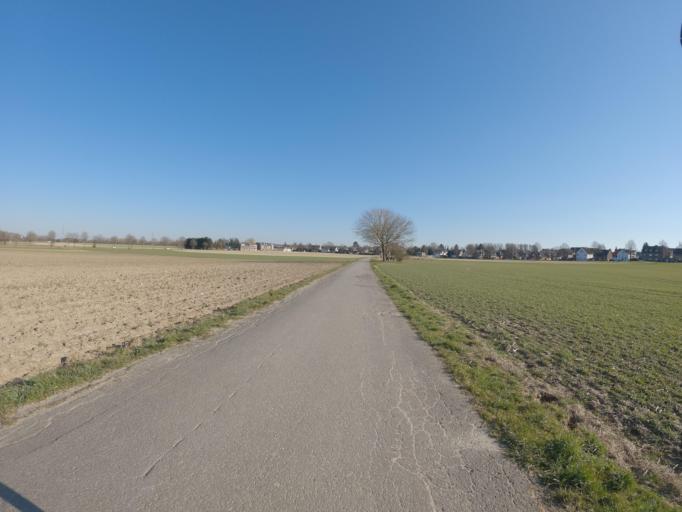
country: NL
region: Limburg
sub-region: Gemeente Kerkrade
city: Kerkrade
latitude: 50.8201
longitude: 6.0512
